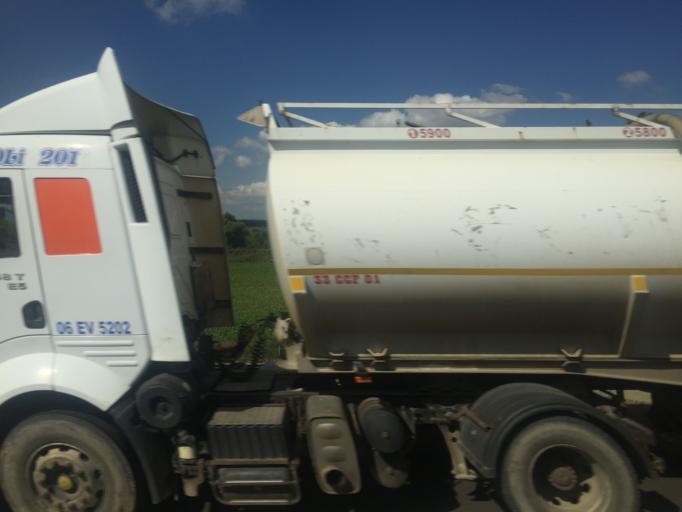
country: TR
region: Bursa
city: Tatkavakli
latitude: 40.1015
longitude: 28.2783
